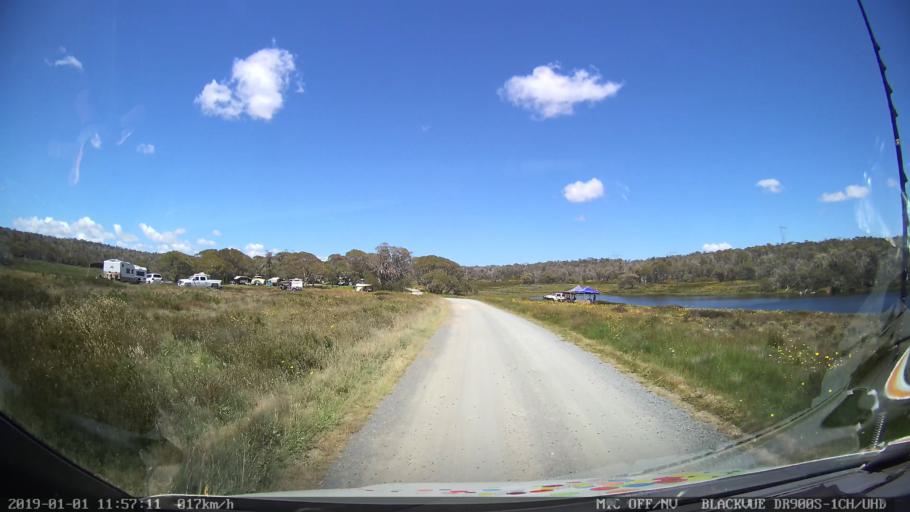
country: AU
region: New South Wales
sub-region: Snowy River
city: Jindabyne
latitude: -35.8872
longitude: 148.4497
